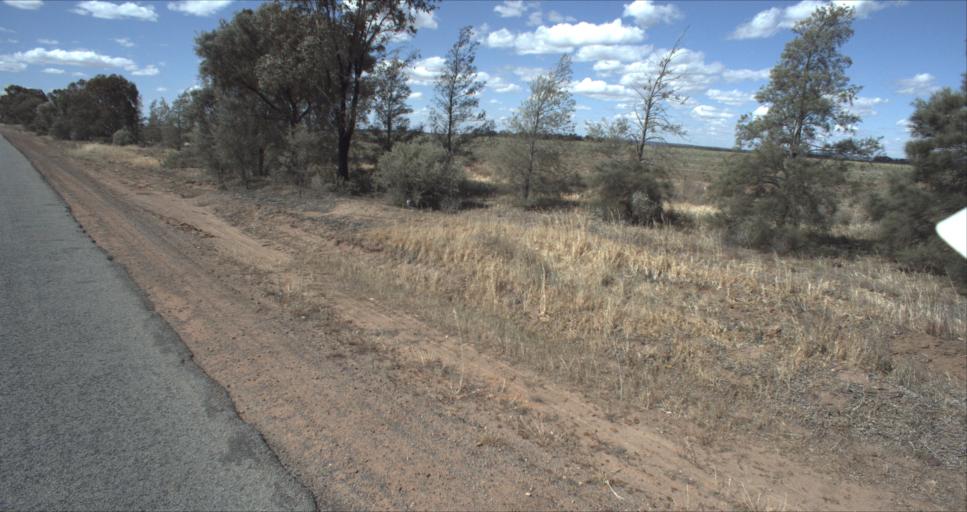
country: AU
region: New South Wales
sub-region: Leeton
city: Leeton
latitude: -34.4772
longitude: 146.2498
